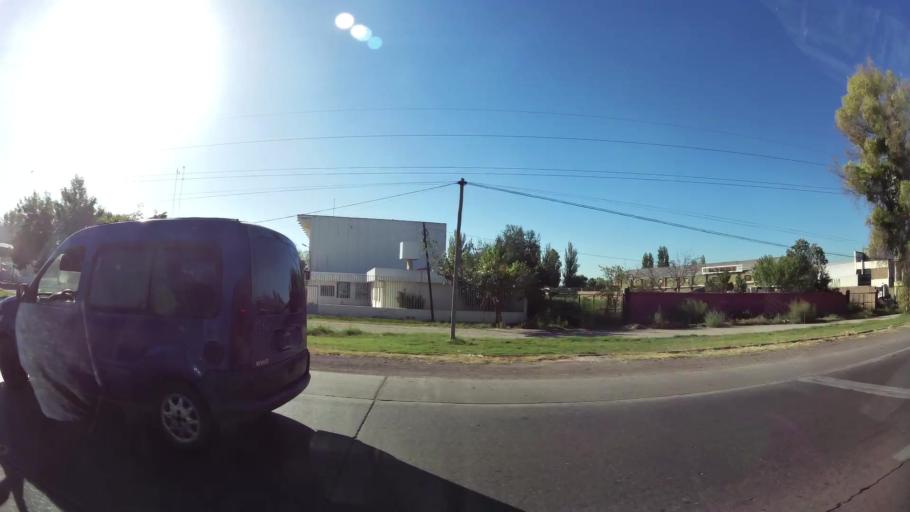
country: AR
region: Mendoza
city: Las Heras
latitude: -32.8496
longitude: -68.8042
